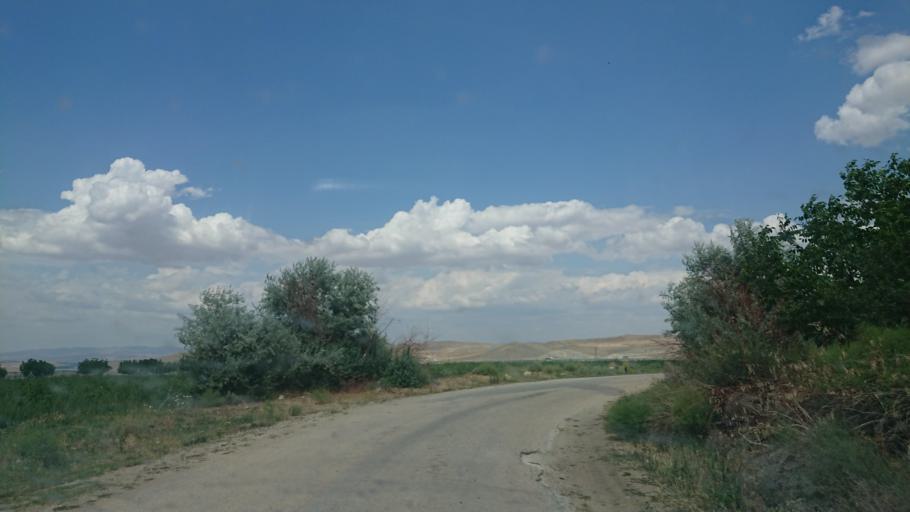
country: TR
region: Aksaray
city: Sariyahsi
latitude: 38.9681
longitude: 33.8915
